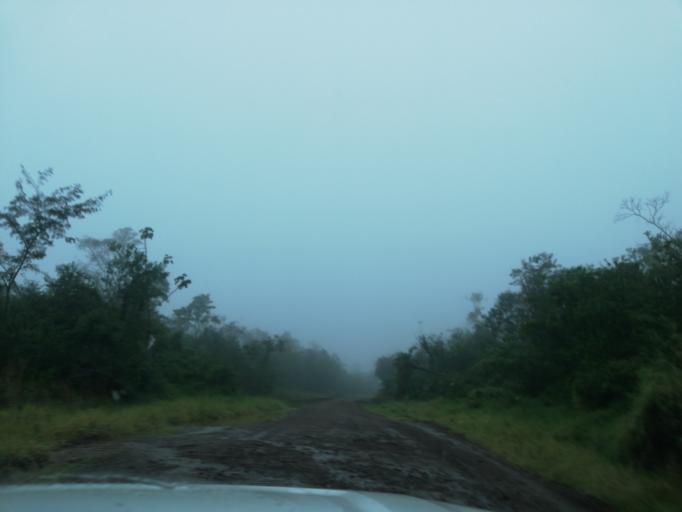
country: AR
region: Misiones
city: Almafuerte
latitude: -27.5248
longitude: -55.4048
